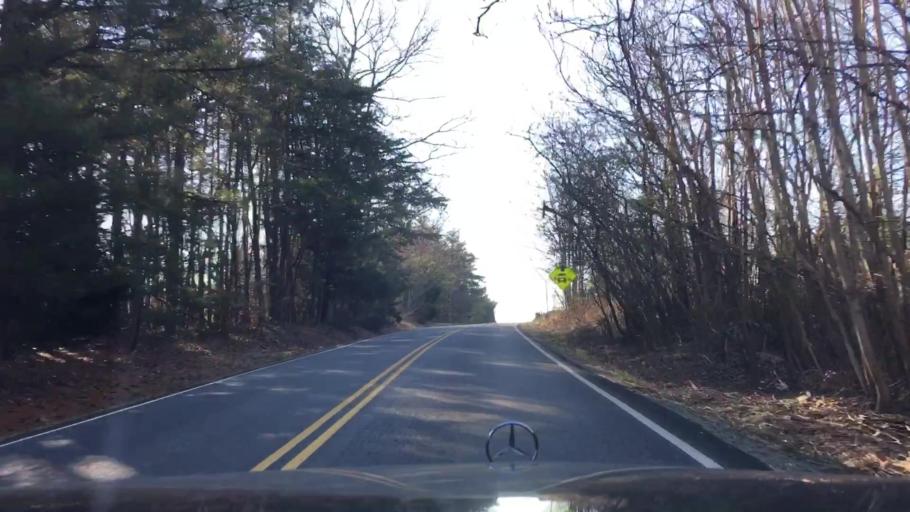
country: US
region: Virginia
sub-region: City of Bedford
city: Bedford
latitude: 37.2096
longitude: -79.4300
